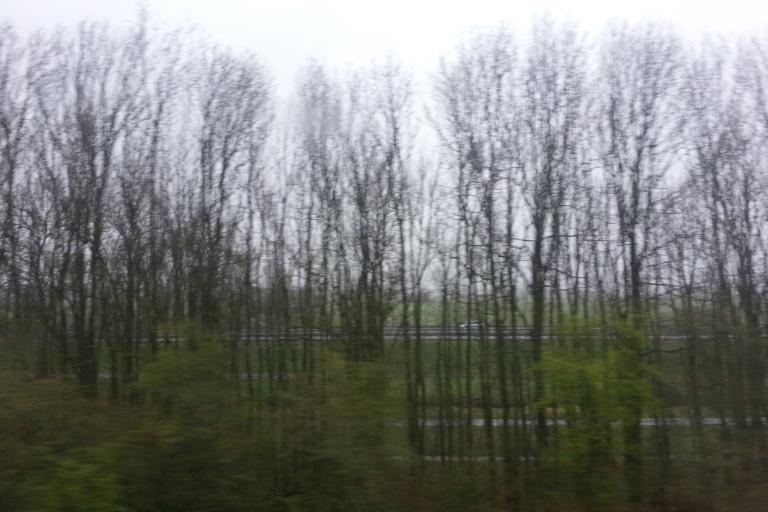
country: NL
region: South Holland
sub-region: Gemeente Teylingen
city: Sassenheim
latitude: 52.2218
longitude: 4.5485
